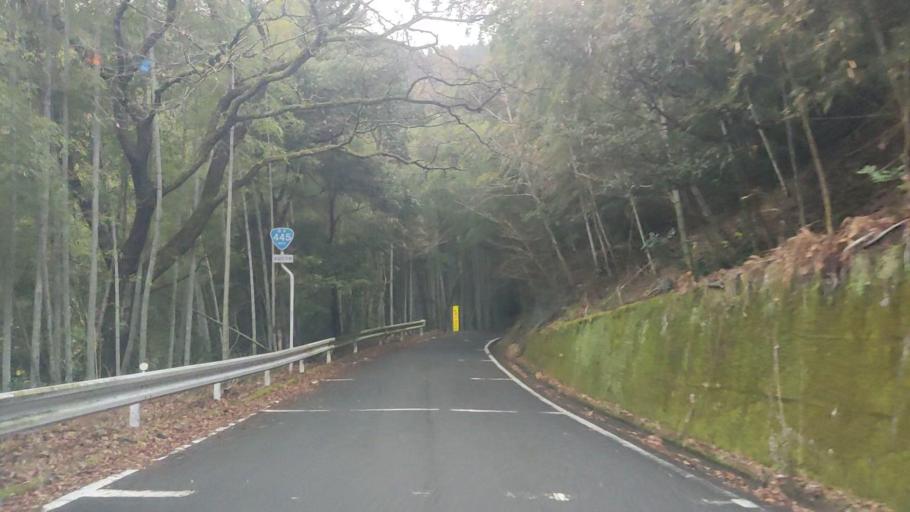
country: JP
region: Kumamoto
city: Matsubase
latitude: 32.5925
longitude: 130.8852
